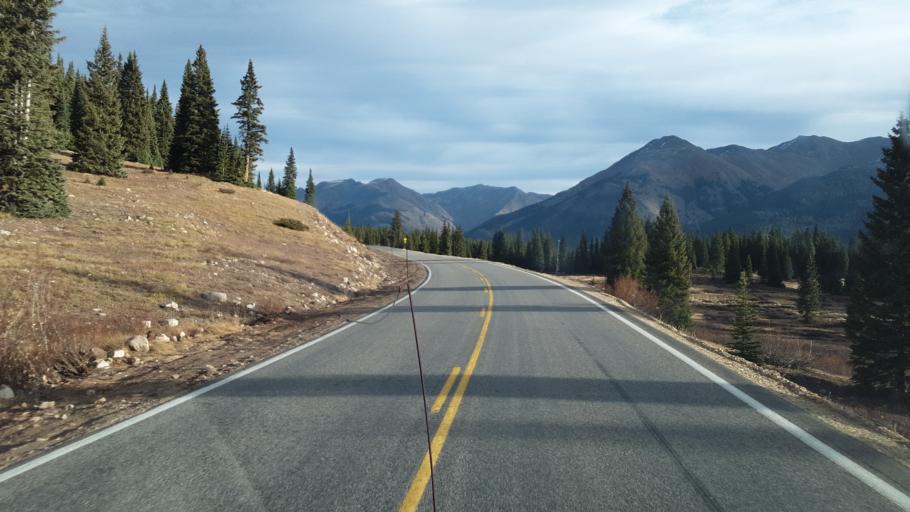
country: US
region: Colorado
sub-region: San Juan County
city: Silverton
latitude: 37.7546
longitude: -107.6816
